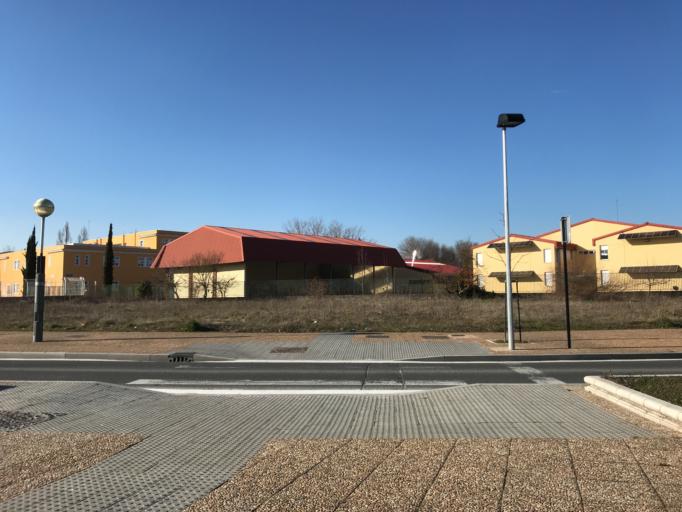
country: ES
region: Basque Country
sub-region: Provincia de Alava
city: Gasteiz / Vitoria
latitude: 42.8349
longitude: -2.6773
